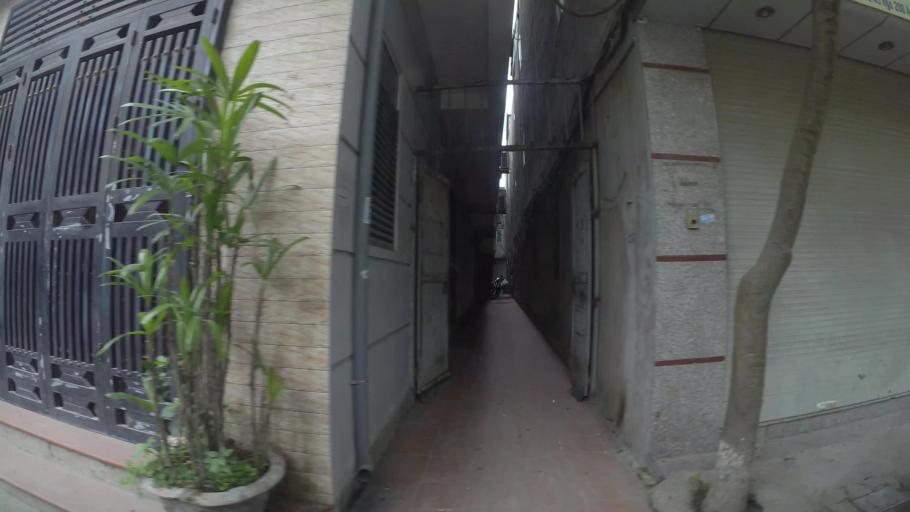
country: VN
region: Ha Noi
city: Tay Ho
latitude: 21.0658
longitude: 105.8316
